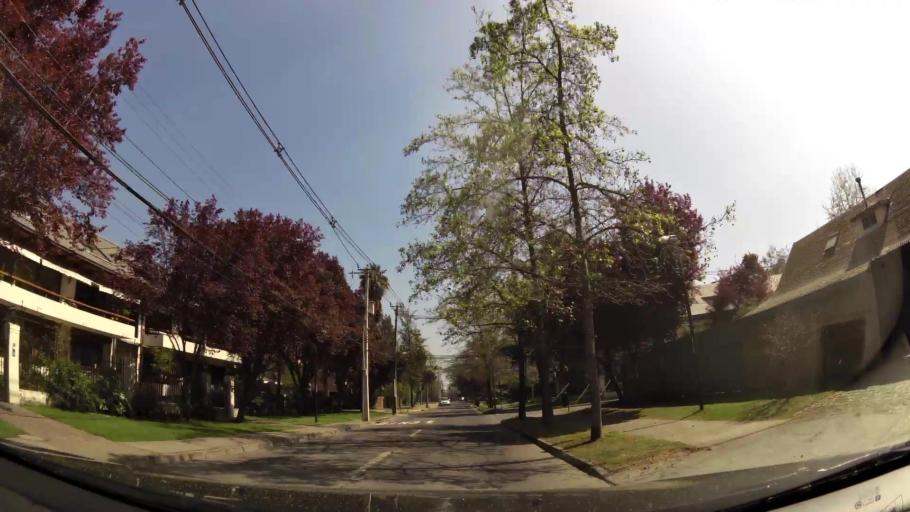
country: CL
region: Santiago Metropolitan
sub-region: Provincia de Santiago
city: Villa Presidente Frei, Nunoa, Santiago, Chile
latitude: -33.3846
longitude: -70.5772
